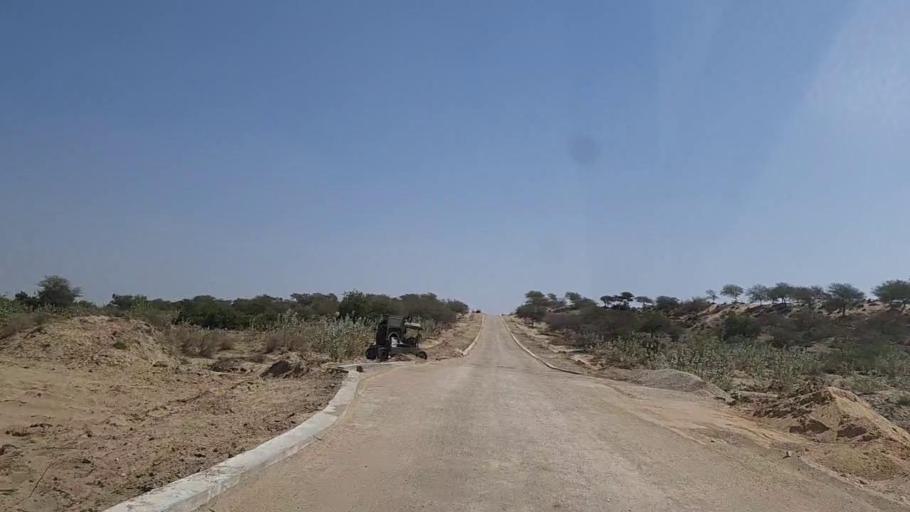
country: PK
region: Sindh
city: Diplo
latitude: 24.4782
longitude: 69.5040
